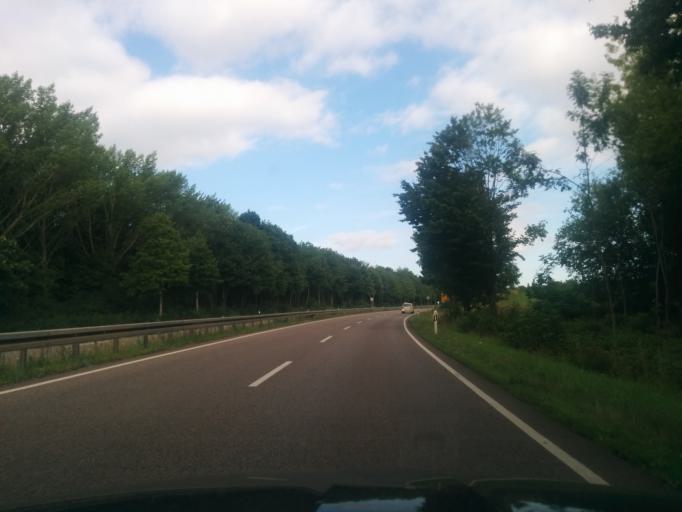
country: DE
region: Saxony-Anhalt
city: Zscherben
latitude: 51.4776
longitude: 11.8888
